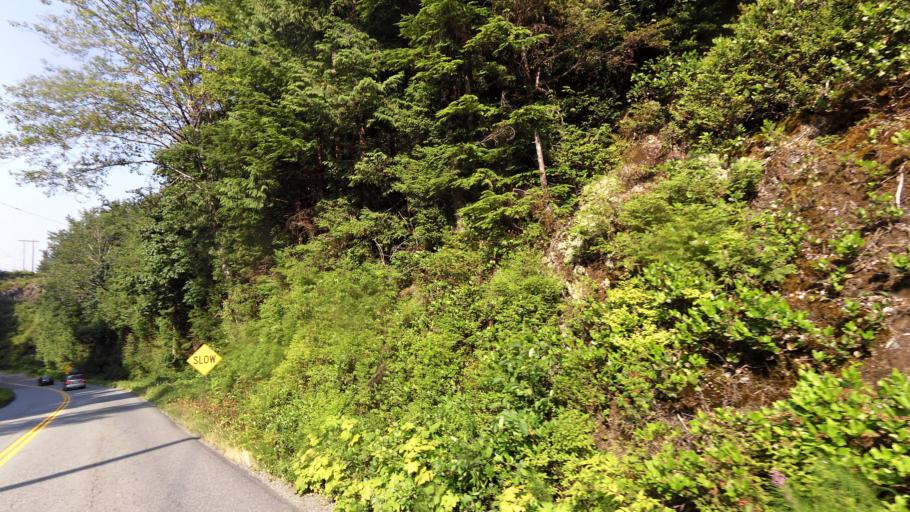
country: CA
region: British Columbia
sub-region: Regional District of Alberni-Clayoquot
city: Ucluelet
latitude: 49.0924
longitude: -125.4523
